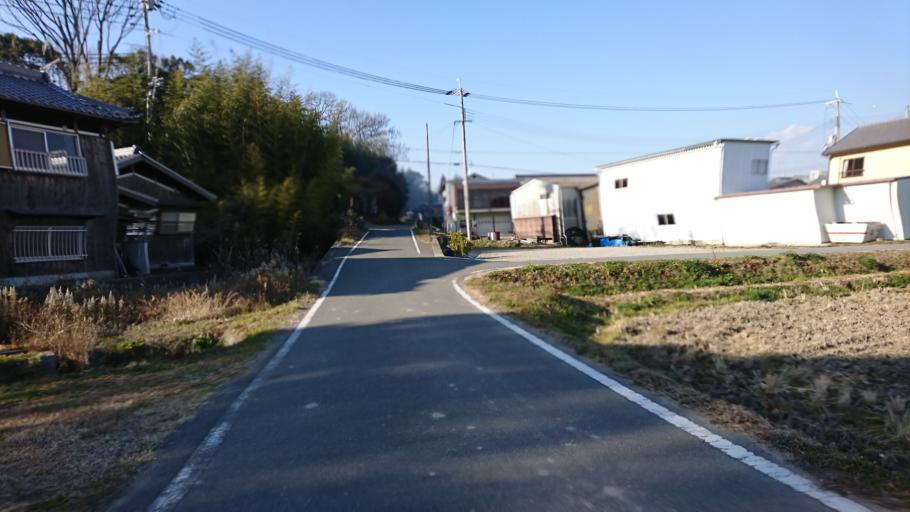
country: JP
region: Hyogo
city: Kakogawacho-honmachi
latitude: 34.7812
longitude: 134.8682
